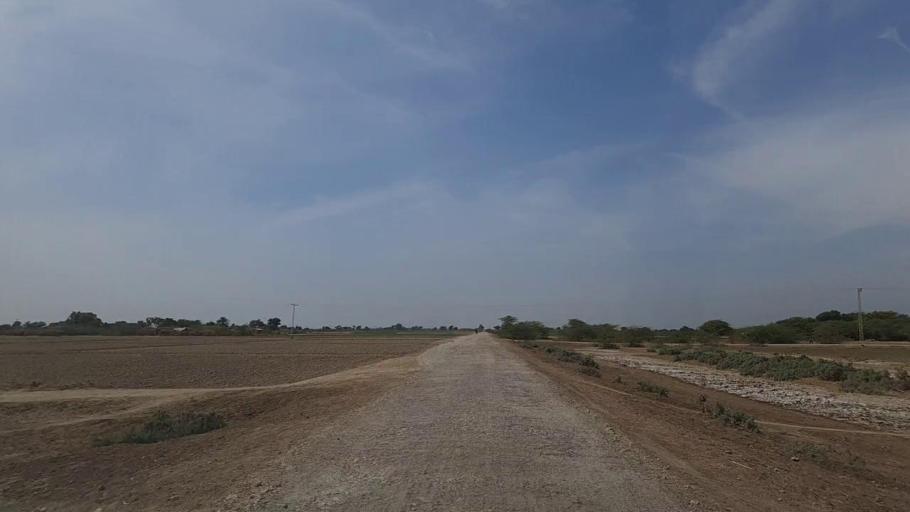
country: PK
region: Sindh
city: Kunri
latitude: 25.2127
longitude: 69.4973
